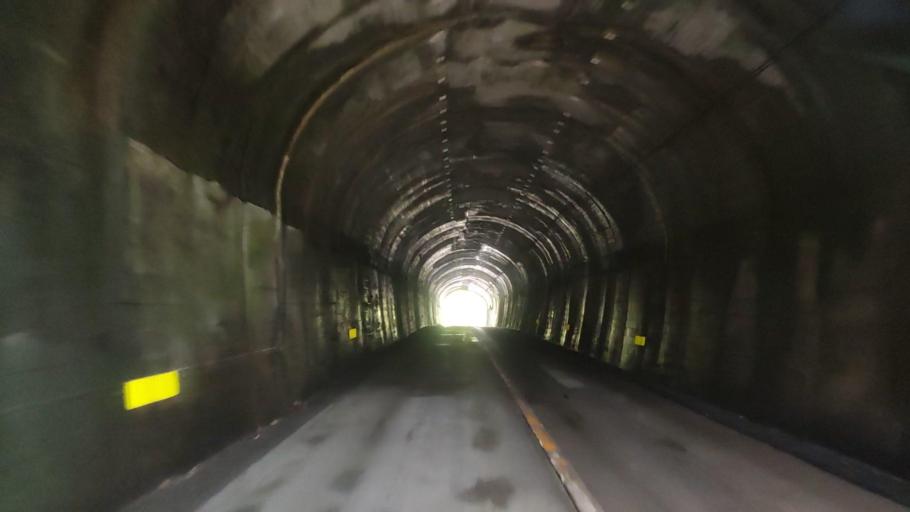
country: JP
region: Mie
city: Ise
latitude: 34.2922
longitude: 136.5314
